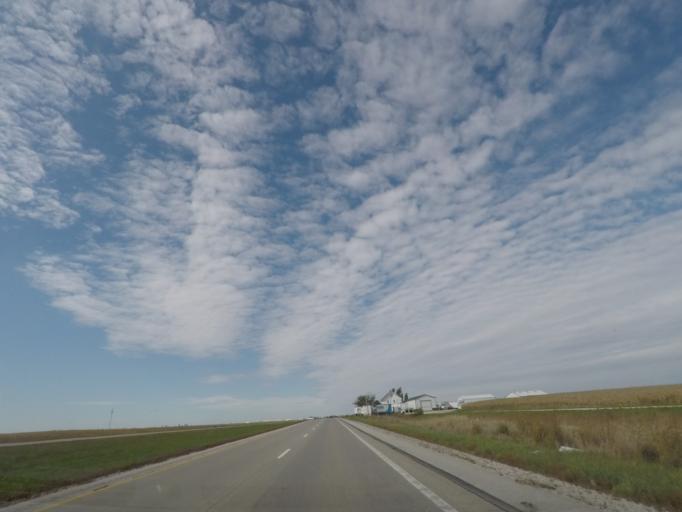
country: US
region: Iowa
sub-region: Story County
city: Ames
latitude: 42.0233
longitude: -93.7441
